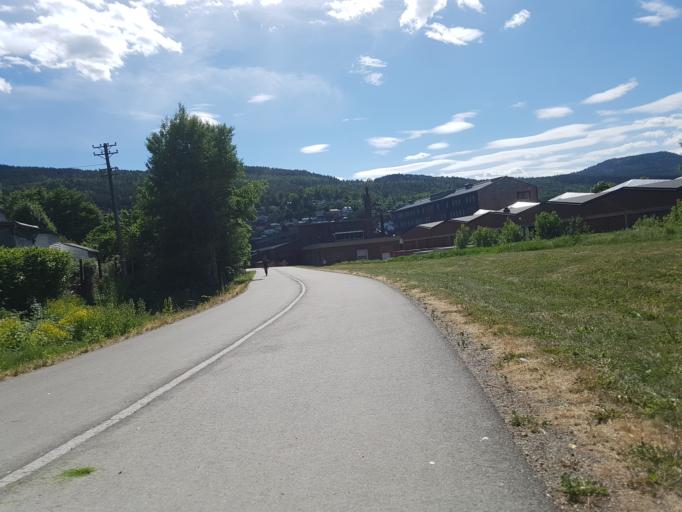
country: NO
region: Buskerud
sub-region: Drammen
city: Drammen
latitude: 59.7415
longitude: 10.1842
